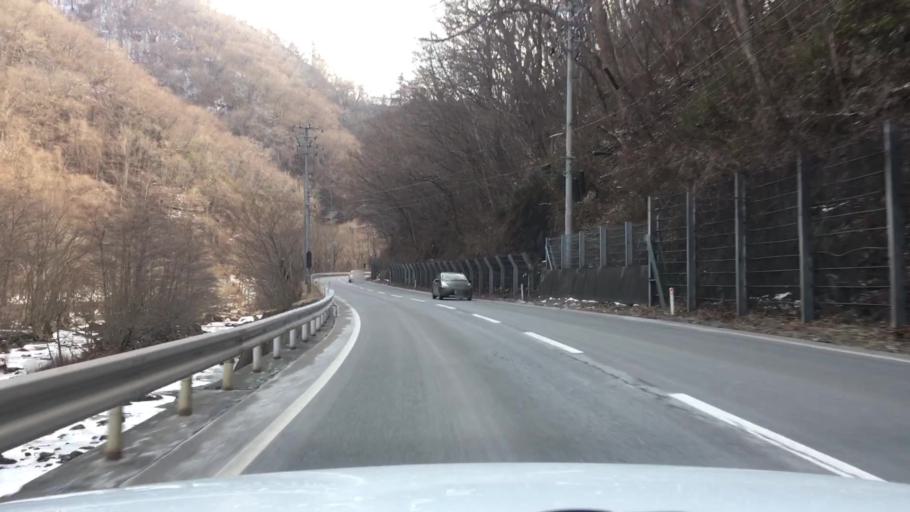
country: JP
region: Iwate
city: Tono
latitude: 39.6377
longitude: 141.5365
